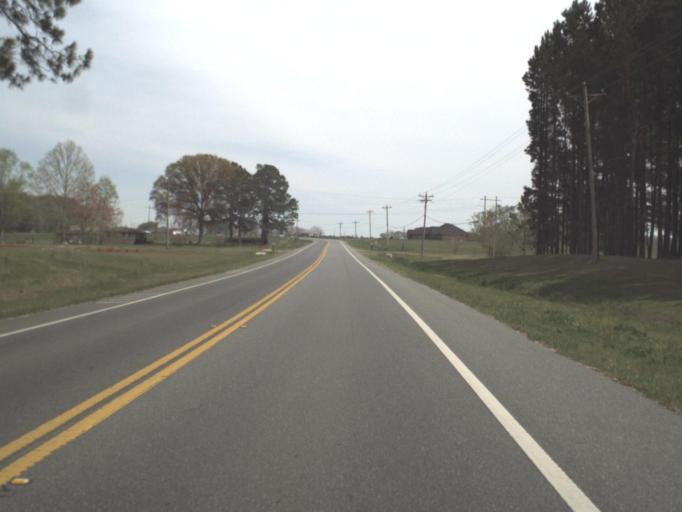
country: US
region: Florida
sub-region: Jackson County
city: Graceville
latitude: 30.9632
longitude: -85.5897
